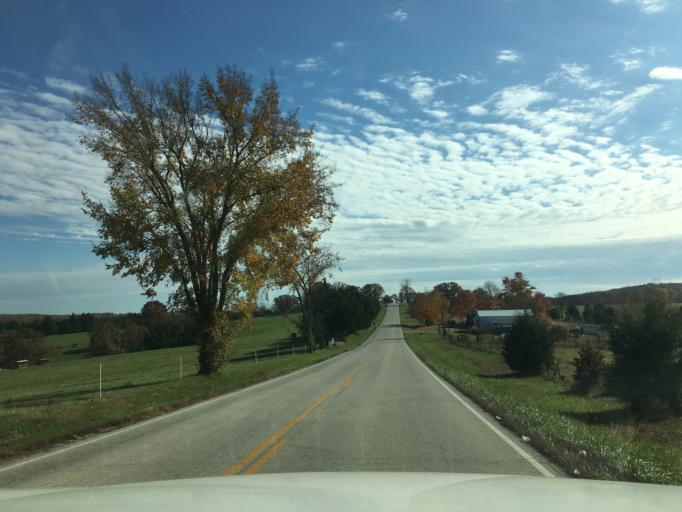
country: US
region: Missouri
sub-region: Maries County
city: Belle
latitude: 38.3466
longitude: -91.7943
